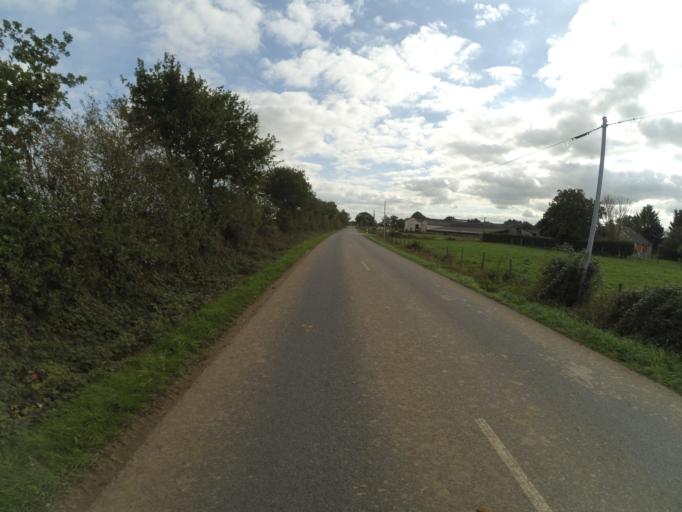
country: FR
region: Pays de la Loire
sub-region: Departement de la Loire-Atlantique
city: Fay-de-Bretagne
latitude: 47.4467
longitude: -1.8163
